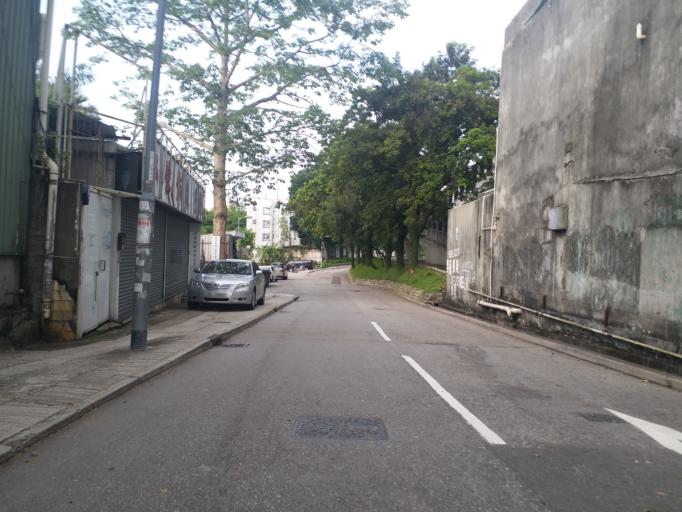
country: HK
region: Yuen Long
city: Yuen Long Kau Hui
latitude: 22.4428
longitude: 114.0112
